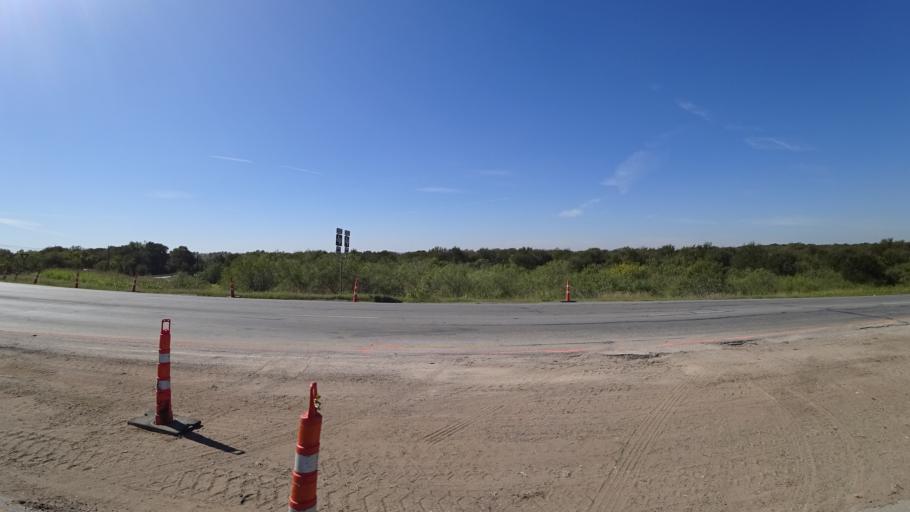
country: US
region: Texas
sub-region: Travis County
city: Hornsby Bend
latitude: 30.2574
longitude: -97.6121
